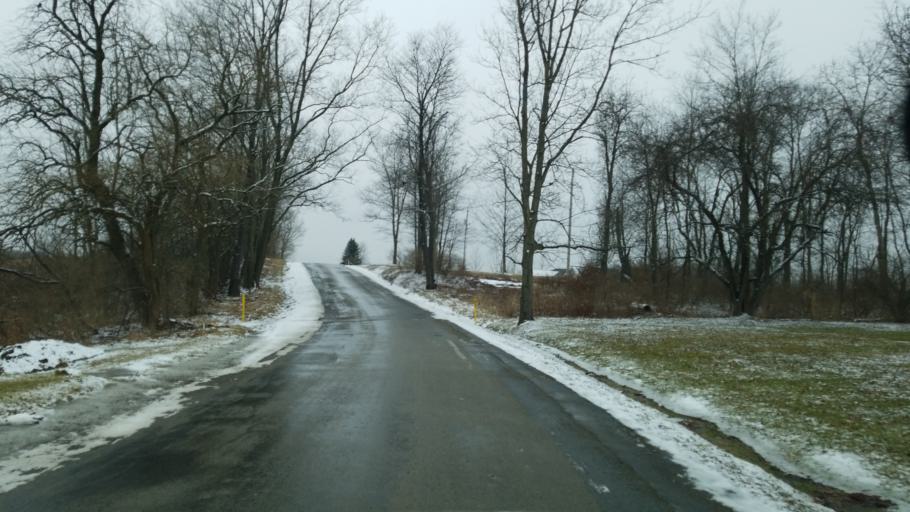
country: US
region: Pennsylvania
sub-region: Jefferson County
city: Sykesville
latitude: 41.0851
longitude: -78.8415
